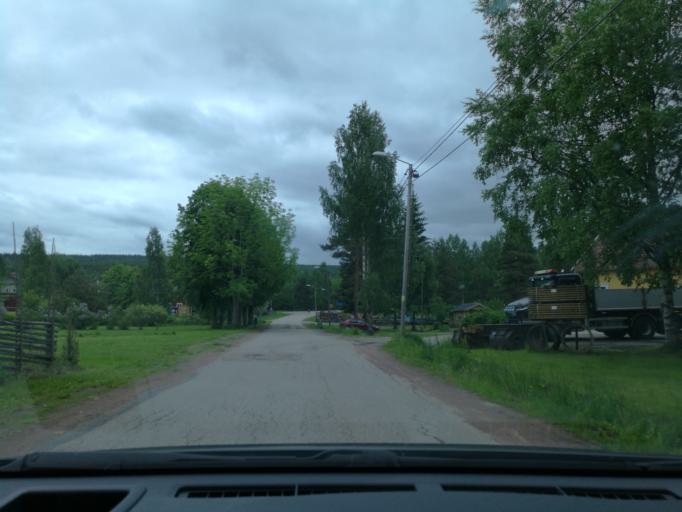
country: SE
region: Dalarna
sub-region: Smedjebackens Kommun
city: Smedjebacken
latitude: 60.1408
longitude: 15.3088
